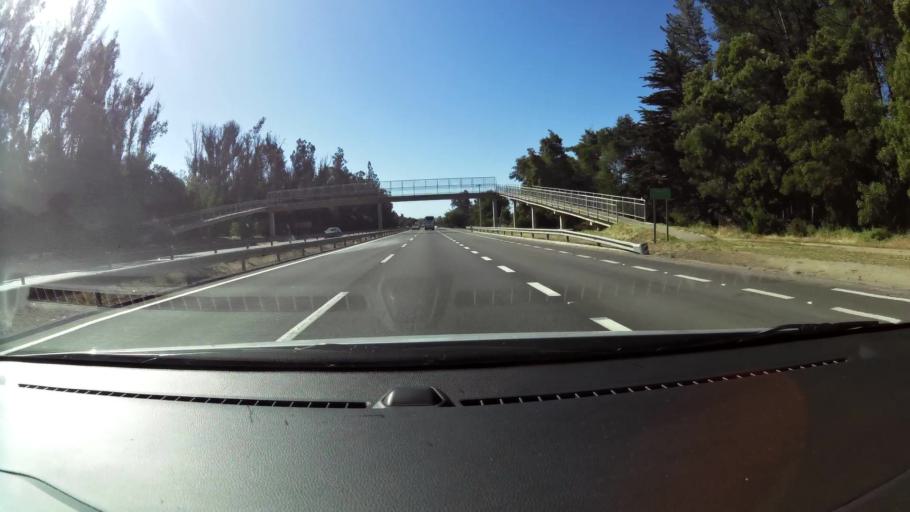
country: CL
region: Valparaiso
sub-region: Provincia de Marga Marga
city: Quilpue
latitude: -33.1913
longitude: -71.4971
